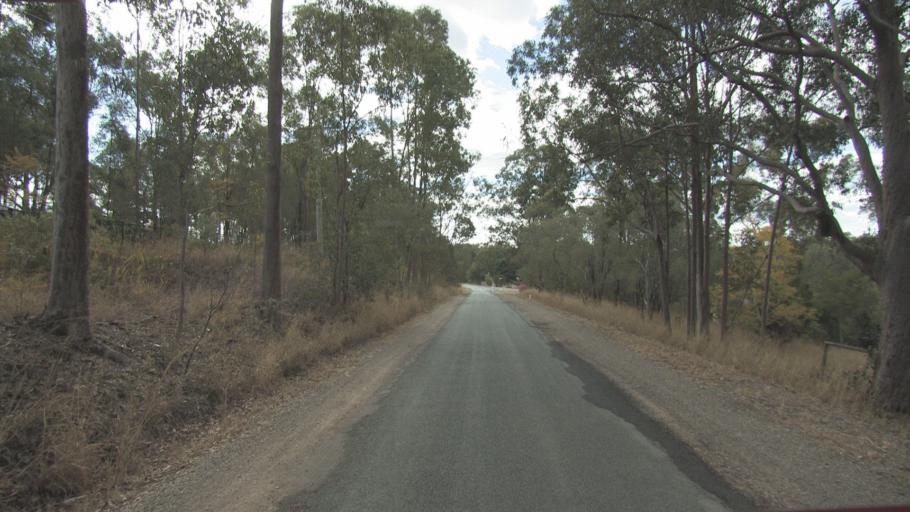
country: AU
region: Queensland
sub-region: Logan
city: Cedar Vale
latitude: -27.8836
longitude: 153.0277
